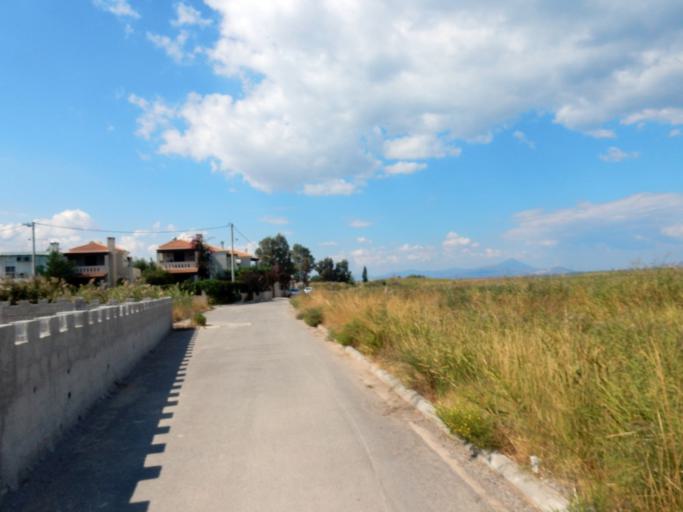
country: GR
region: Attica
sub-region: Nomarchia Anatolikis Attikis
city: Skala Oropou
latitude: 38.3339
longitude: 23.7753
